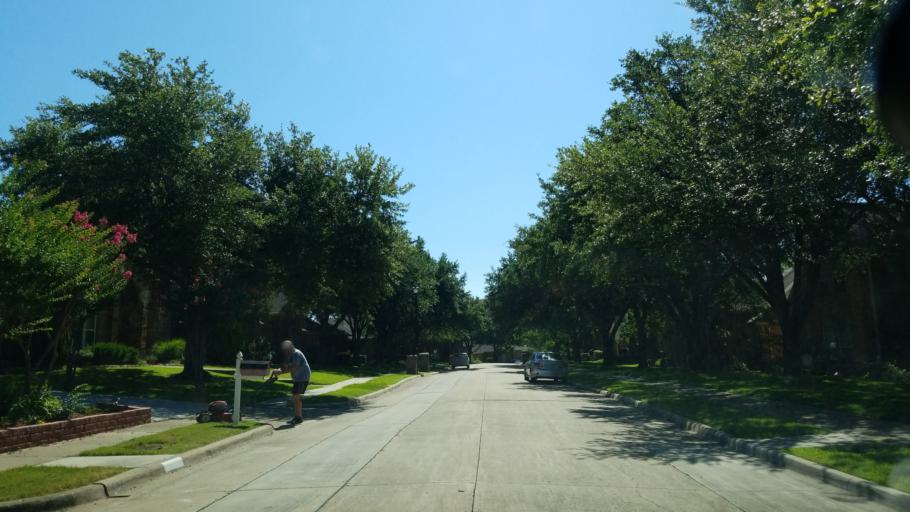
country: US
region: Texas
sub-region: Dallas County
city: Carrollton
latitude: 32.9680
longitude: -96.8842
